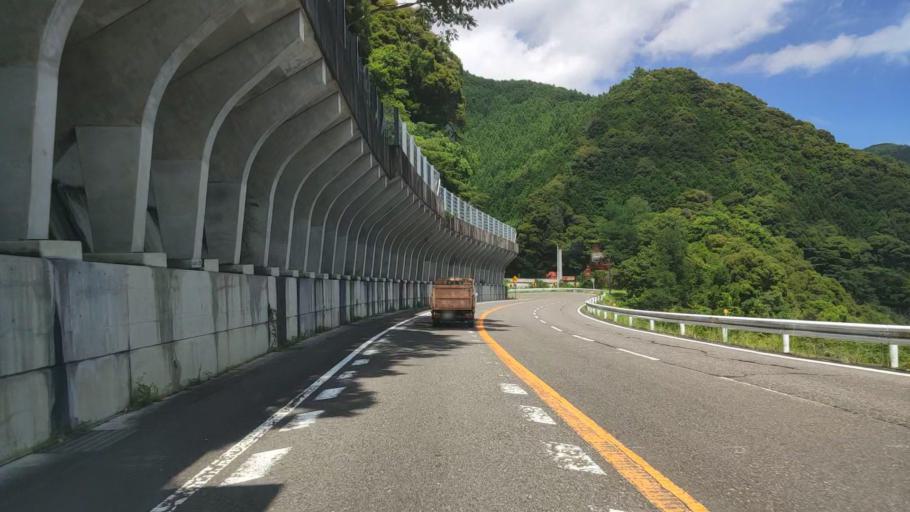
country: JP
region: Mie
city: Owase
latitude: 33.9192
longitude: 136.1055
